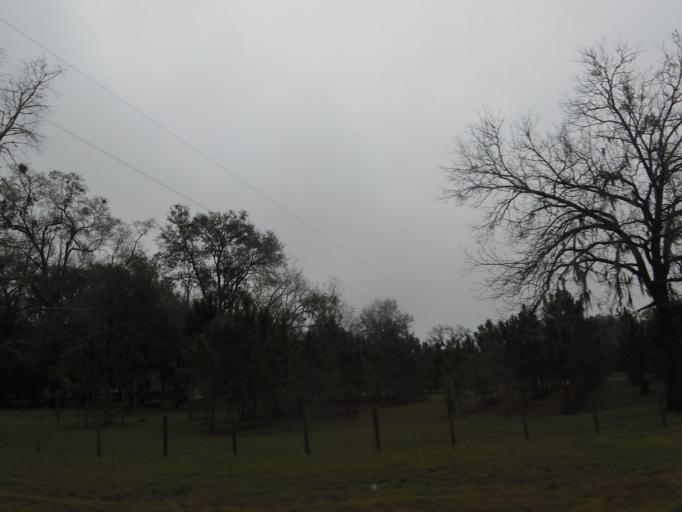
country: US
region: Florida
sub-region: Alachua County
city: High Springs
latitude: 29.8568
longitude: -82.5698
